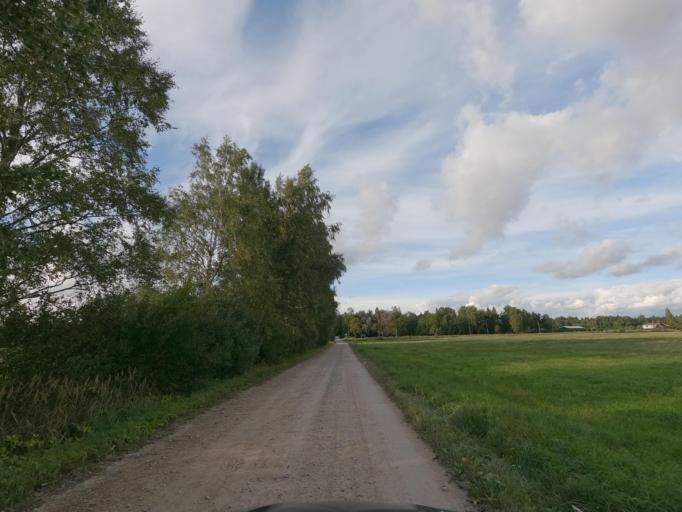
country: EE
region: Raplamaa
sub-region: Rapla vald
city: Rapla
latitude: 59.0180
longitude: 24.7666
